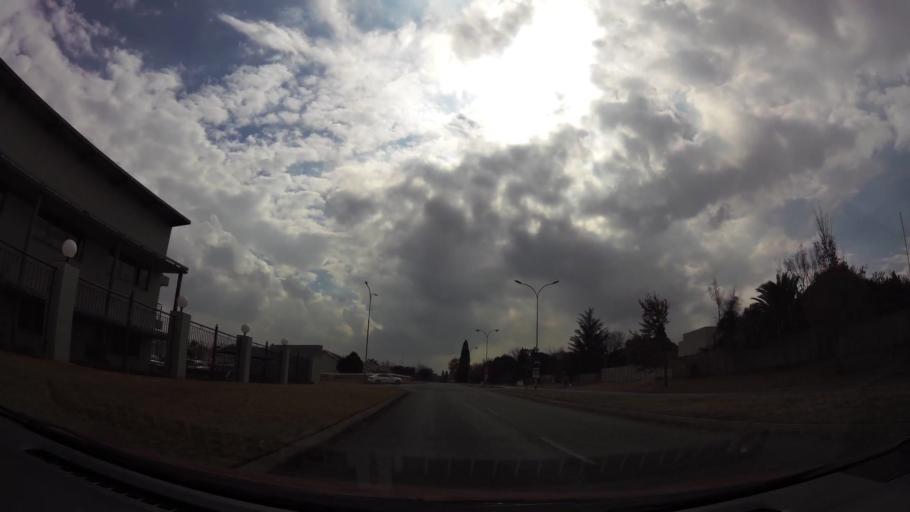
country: ZA
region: Gauteng
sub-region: Sedibeng District Municipality
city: Vanderbijlpark
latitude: -26.7408
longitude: 27.8443
